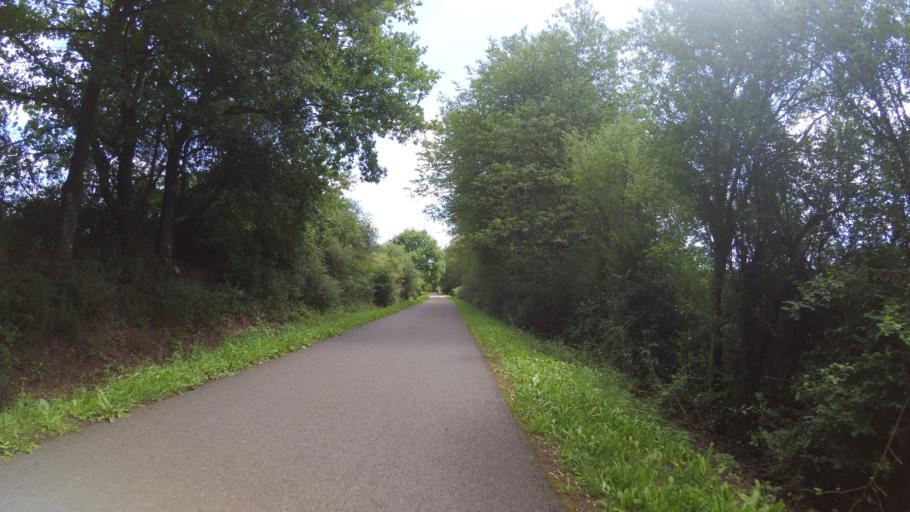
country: DE
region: Saarland
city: Namborn
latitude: 49.4879
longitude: 7.1446
